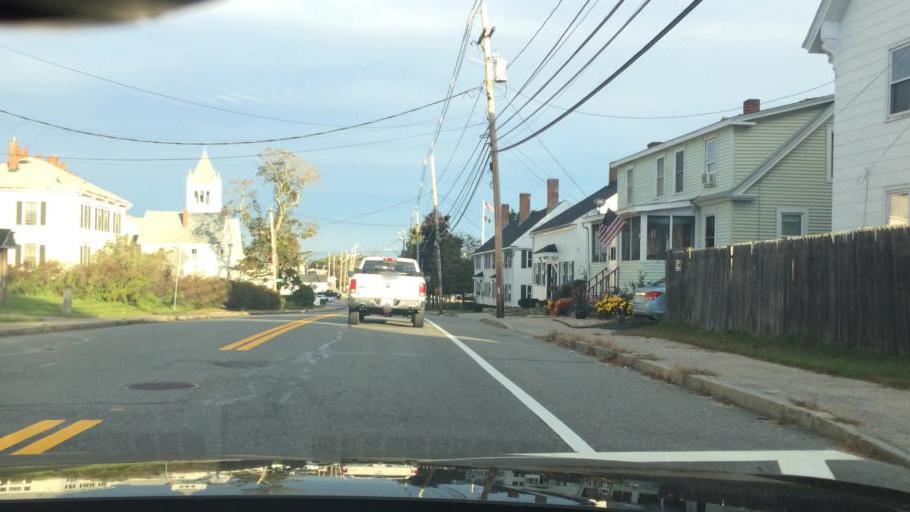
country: US
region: Massachusetts
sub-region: Middlesex County
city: Chelmsford
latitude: 42.6376
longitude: -71.3811
